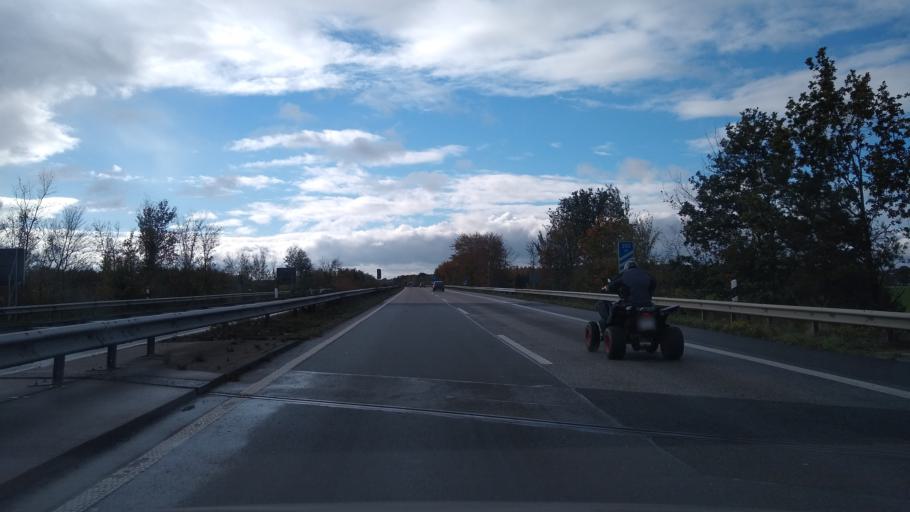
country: DE
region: Lower Saxony
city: Wardenburg
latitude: 53.0515
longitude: 8.2253
